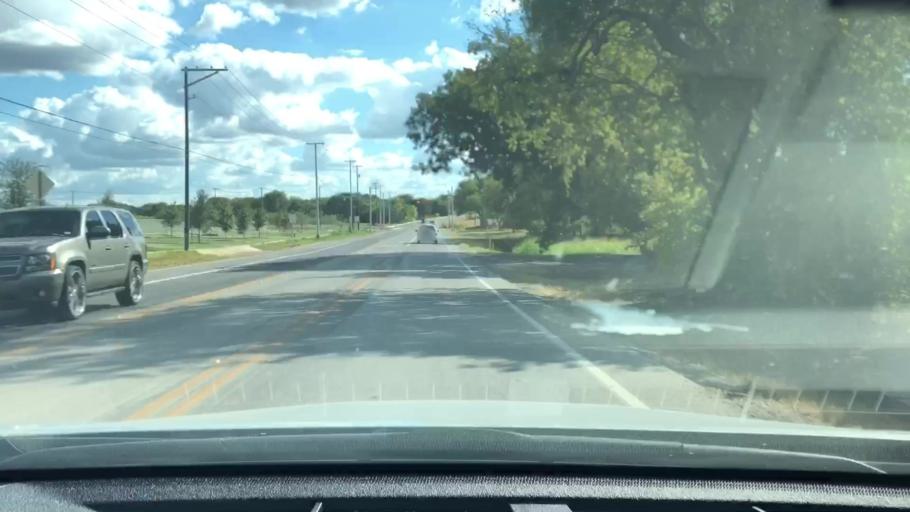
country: US
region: Texas
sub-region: Guadalupe County
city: Northcliff
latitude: 29.6344
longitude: -98.2431
